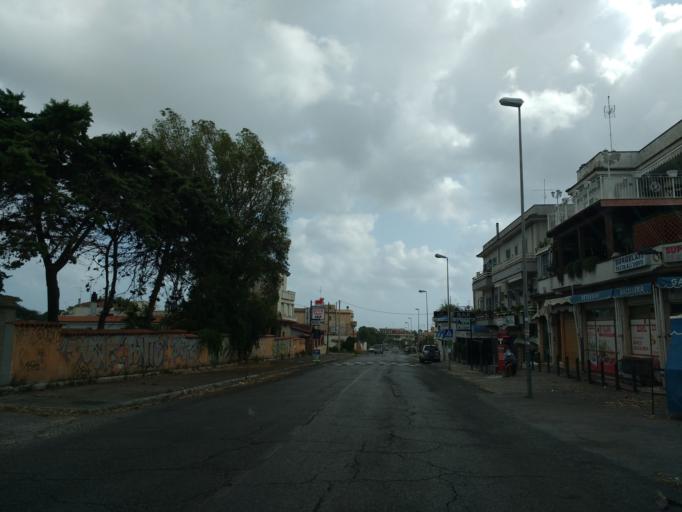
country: IT
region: Latium
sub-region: Citta metropolitana di Roma Capitale
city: Anzio
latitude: 41.4785
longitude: 12.6035
